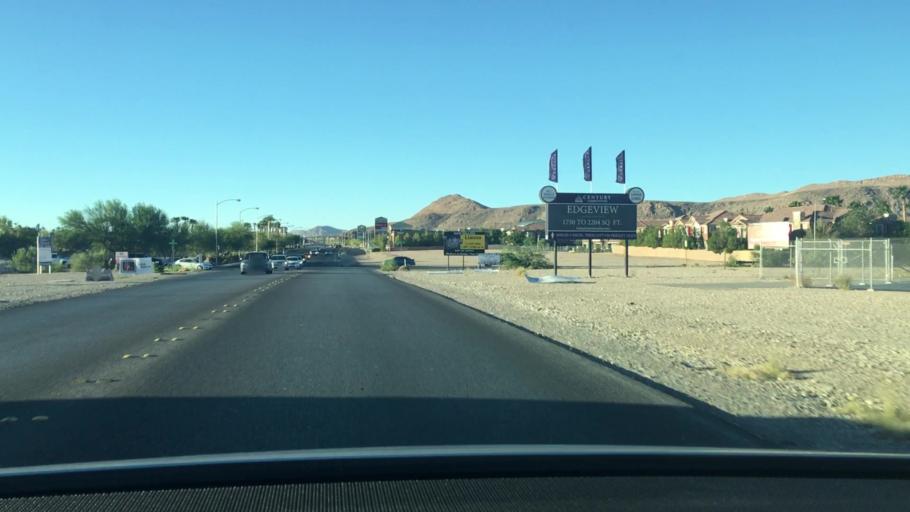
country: US
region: Nevada
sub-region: Clark County
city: Summerlin South
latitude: 36.0750
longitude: -115.2977
